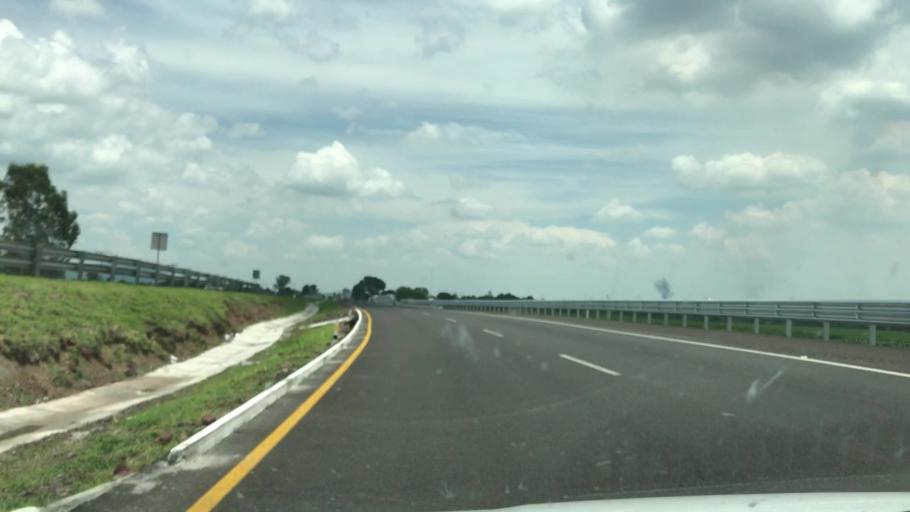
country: MX
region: Guanajuato
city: Salamanca
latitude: 20.6037
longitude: -101.2079
